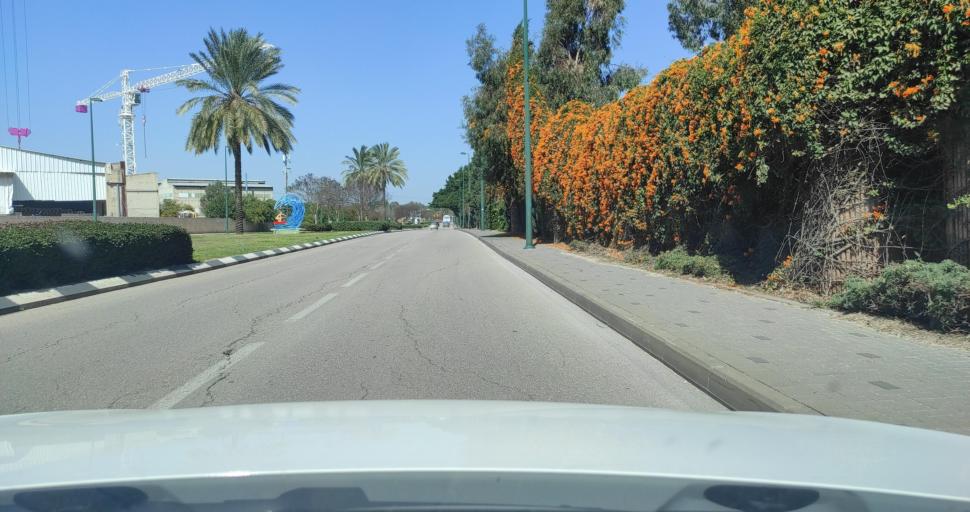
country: IL
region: Central District
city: Bet Yizhaq
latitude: 32.3145
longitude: 34.8789
